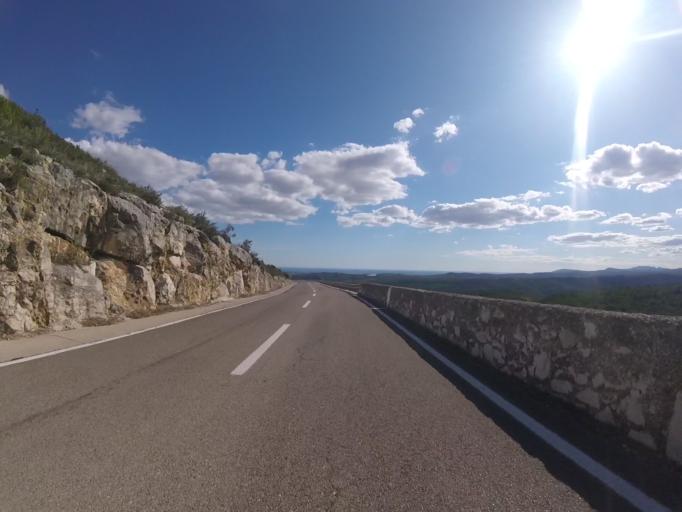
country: ES
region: Valencia
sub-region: Provincia de Castello
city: Alcala de Xivert
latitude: 40.2931
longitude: 0.1812
